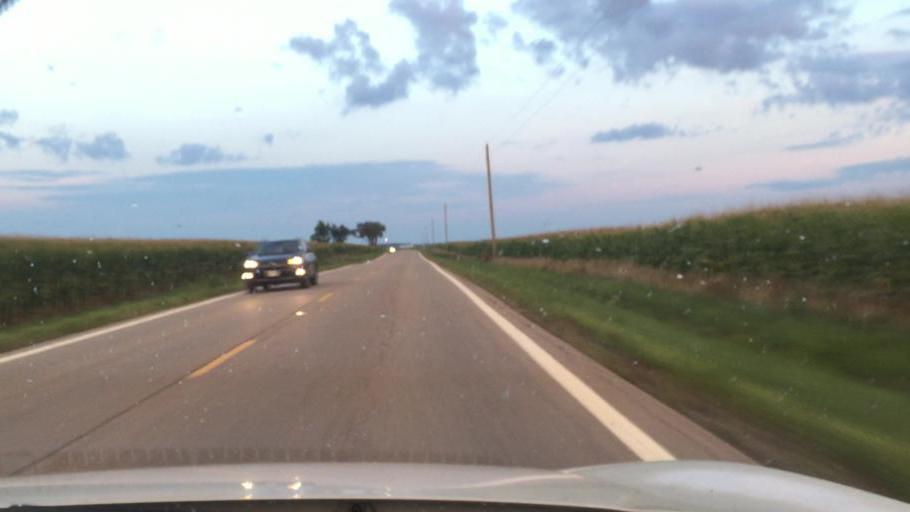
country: US
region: Ohio
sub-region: Madison County
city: Choctaw Lake
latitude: 40.0201
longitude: -83.4703
